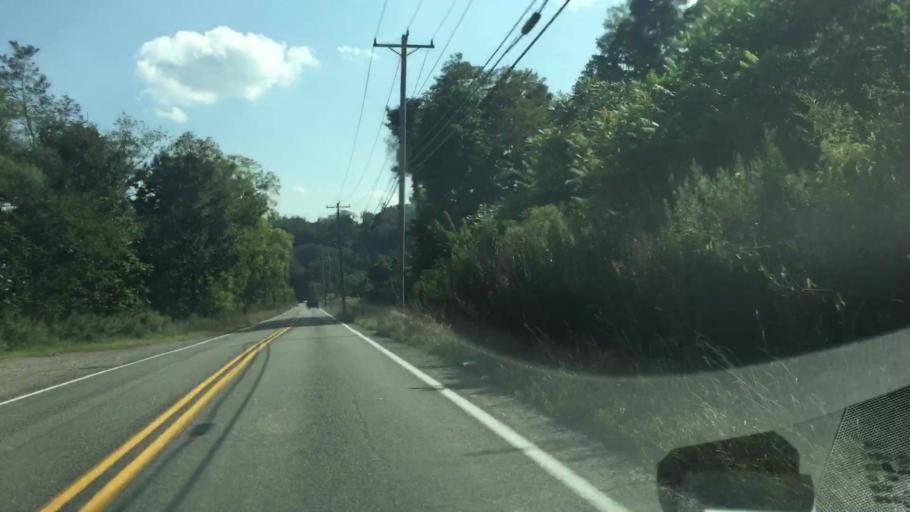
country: US
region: Pennsylvania
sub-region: Allegheny County
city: Franklin Park
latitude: 40.5558
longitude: -80.0865
